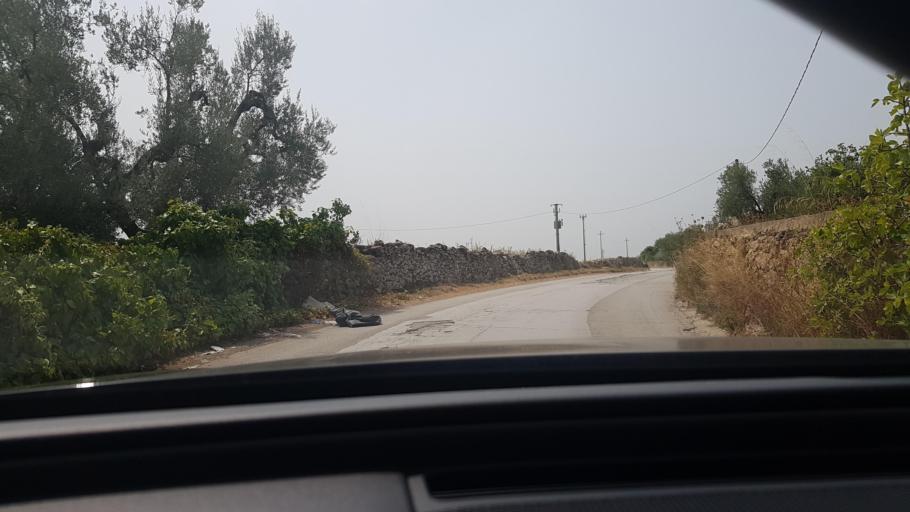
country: IT
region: Apulia
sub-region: Provincia di Barletta - Andria - Trani
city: Andria
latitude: 41.2221
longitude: 16.2653
